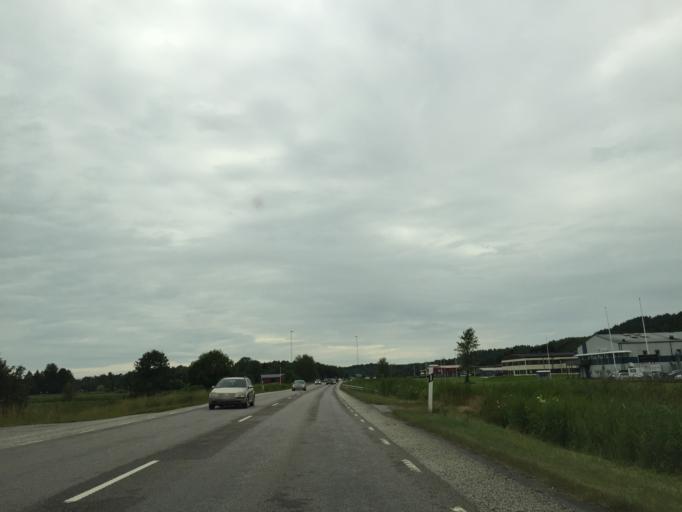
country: SE
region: Vaestra Goetaland
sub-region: Tjorns Kommun
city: Myggenas
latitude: 58.0294
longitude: 11.7154
